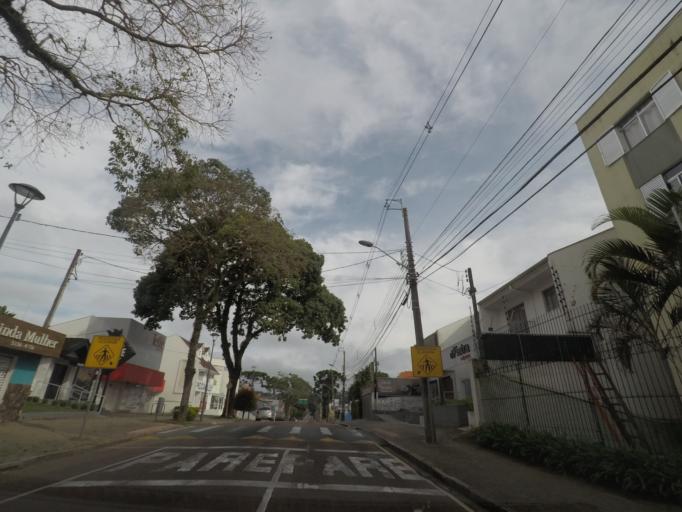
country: BR
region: Parana
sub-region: Curitiba
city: Curitiba
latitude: -25.4149
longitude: -49.2775
